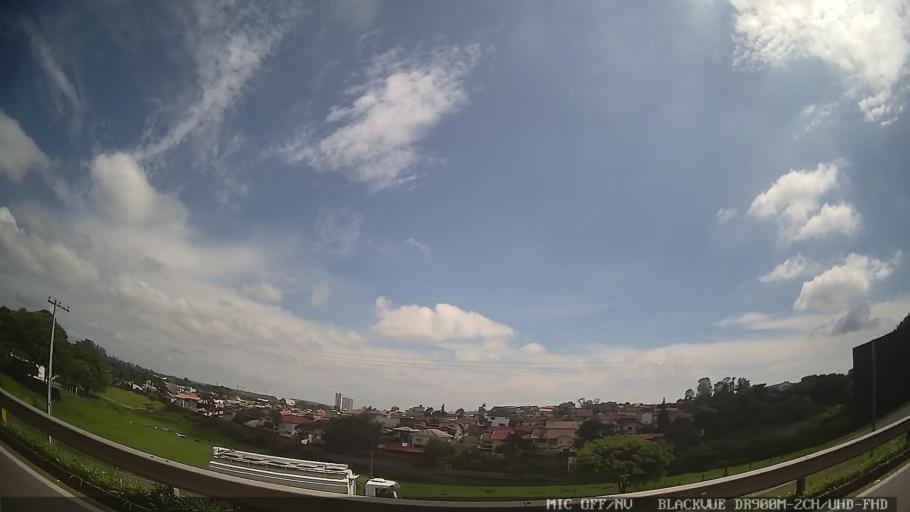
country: BR
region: Sao Paulo
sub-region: Tiete
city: Tiete
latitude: -23.1182
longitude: -47.7154
